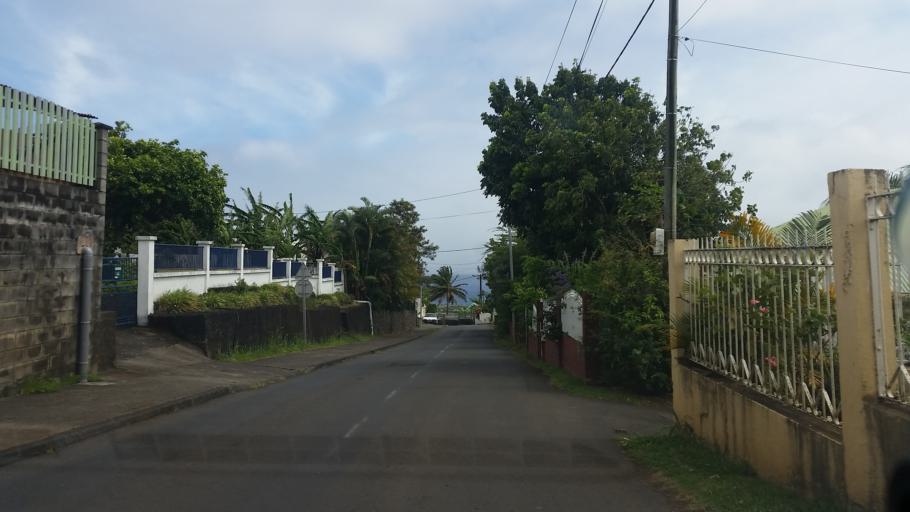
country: RE
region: Reunion
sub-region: Reunion
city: Sainte-Marie
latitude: -20.9190
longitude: 55.5315
